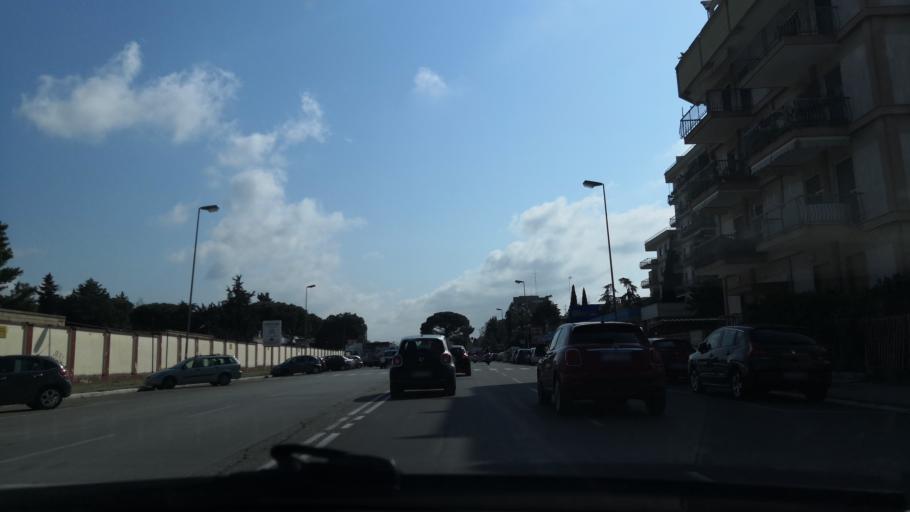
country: IT
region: Apulia
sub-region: Provincia di Bari
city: Bari
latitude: 41.0979
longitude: 16.8737
